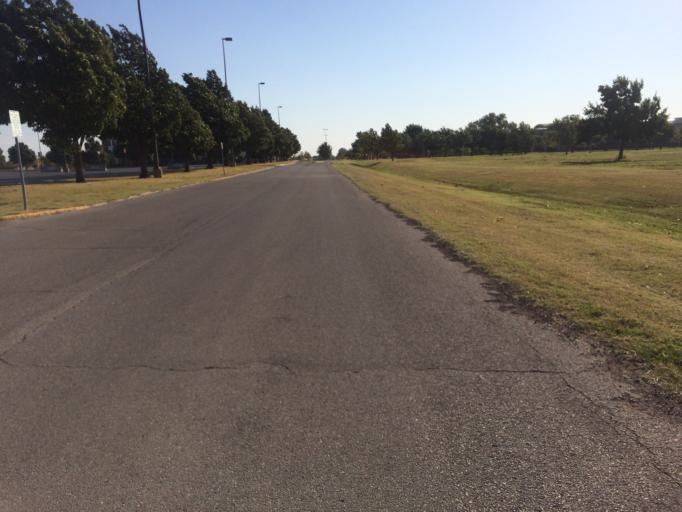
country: US
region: Oklahoma
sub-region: Cleveland County
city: Norman
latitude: 35.1852
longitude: -97.4442
